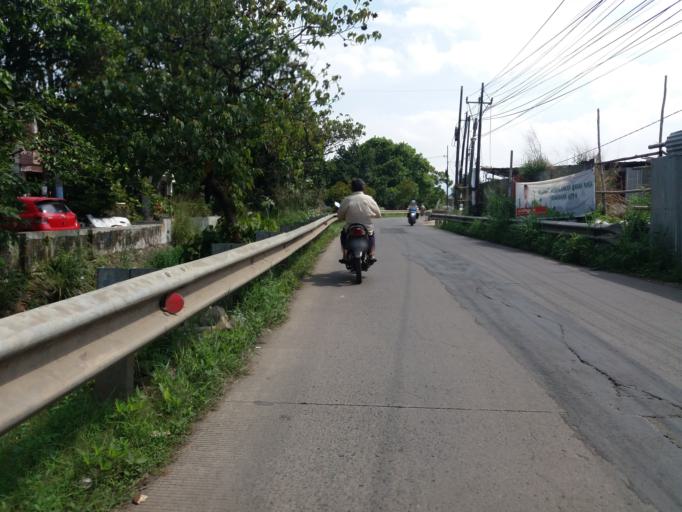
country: ID
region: West Java
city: Bandung
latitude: -6.9223
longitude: 107.6641
